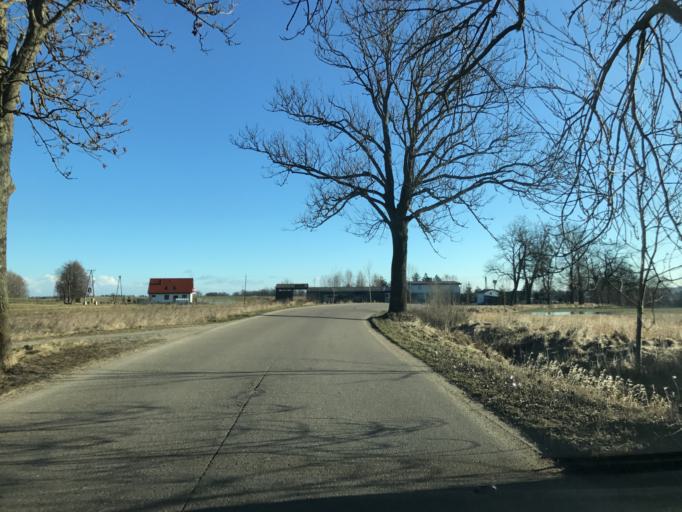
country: PL
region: Warmian-Masurian Voivodeship
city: Dobre Miasto
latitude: 53.9442
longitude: 20.3029
